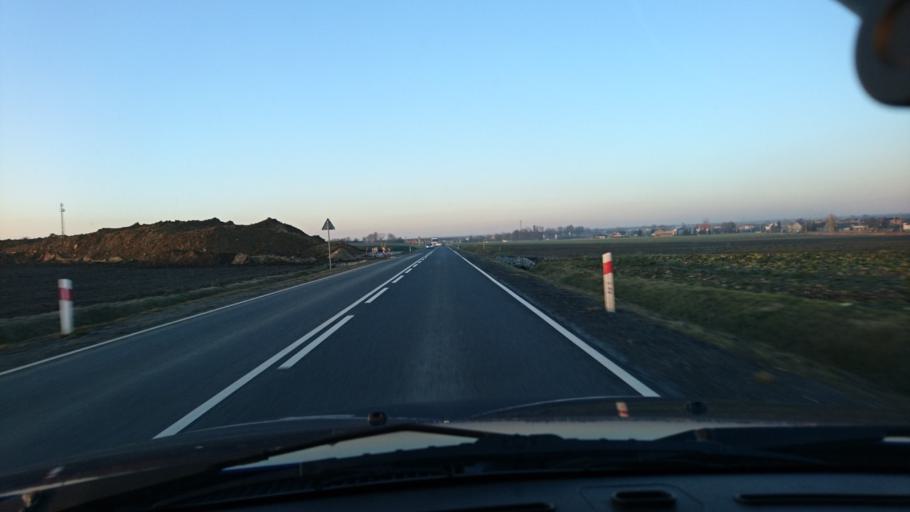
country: PL
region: Silesian Voivodeship
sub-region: Powiat gliwicki
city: Wielowies
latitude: 50.4958
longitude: 18.6070
